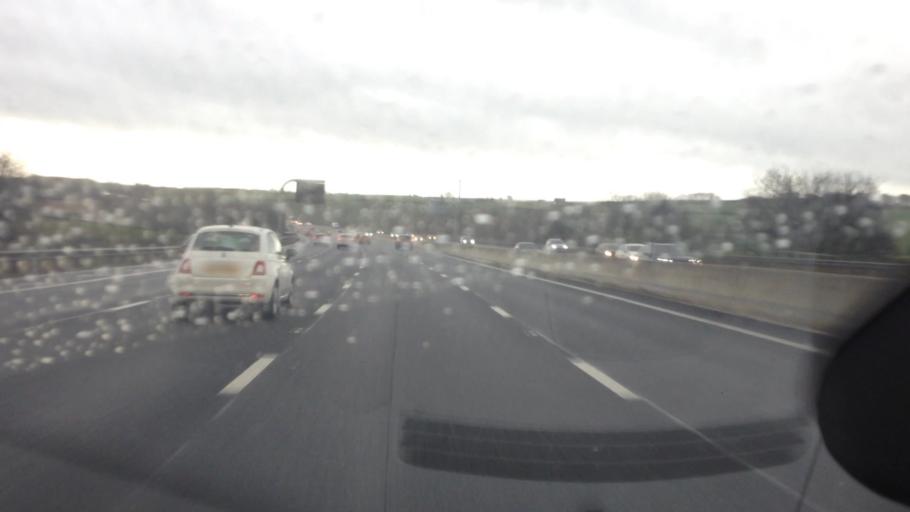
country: GB
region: England
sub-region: City and Borough of Wakefield
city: Ossett
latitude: 53.7004
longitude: -1.5558
